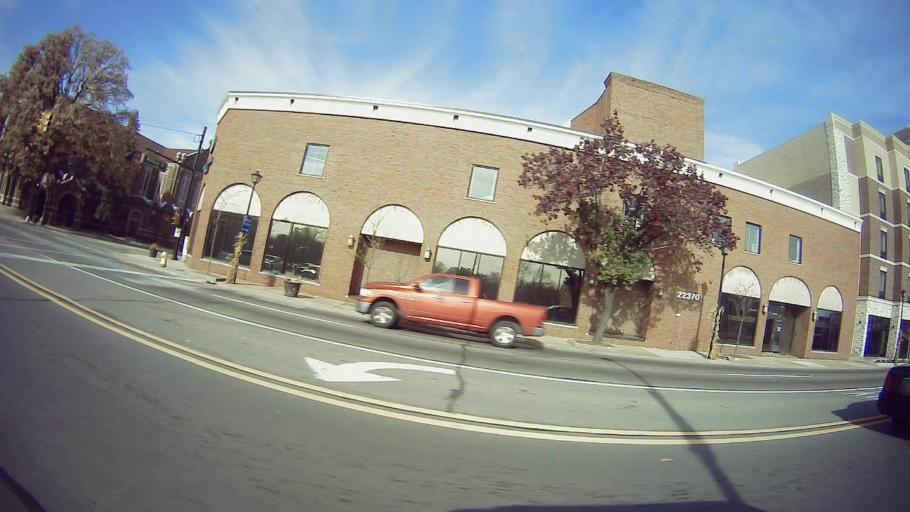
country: US
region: Michigan
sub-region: Wayne County
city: Dearborn Heights
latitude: 42.3046
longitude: -83.2507
